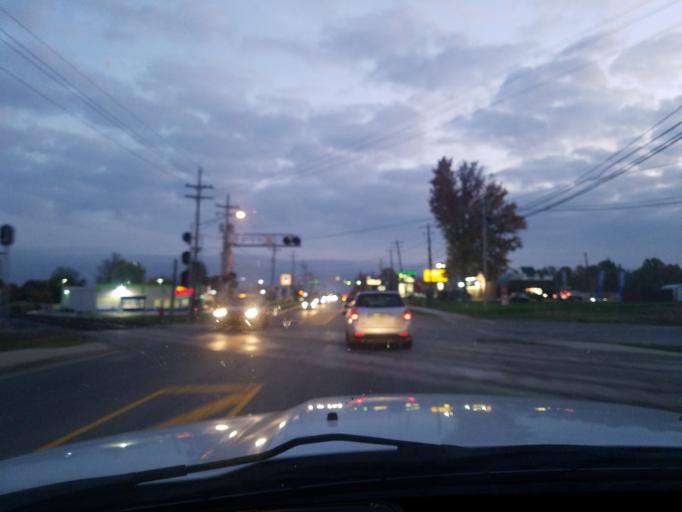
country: US
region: Indiana
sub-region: Floyd County
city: New Albany
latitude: 38.3265
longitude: -85.8192
